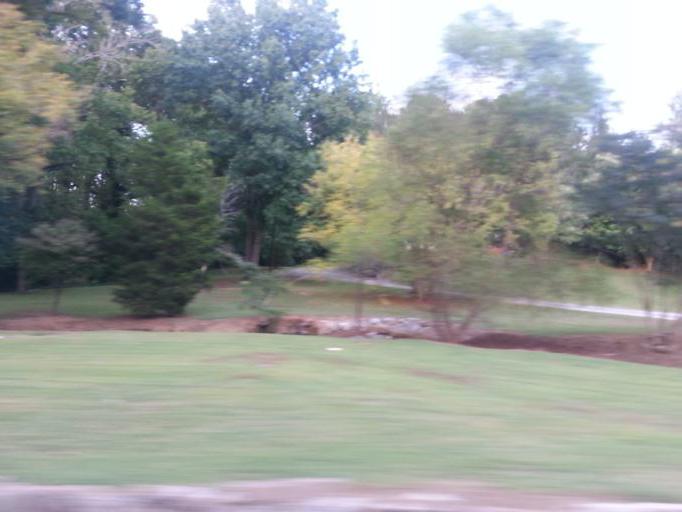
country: US
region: Tennessee
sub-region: Knox County
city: Knoxville
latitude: 35.9289
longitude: -83.9108
